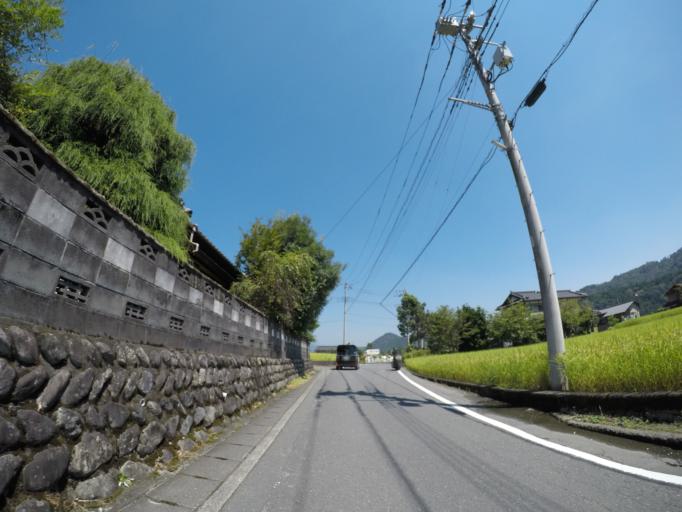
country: JP
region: Shizuoka
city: Fujinomiya
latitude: 35.2113
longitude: 138.5647
